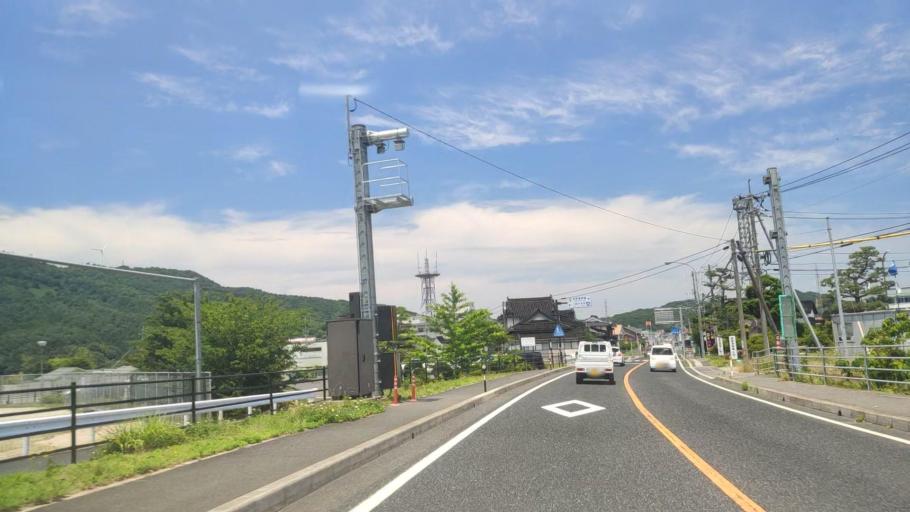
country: JP
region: Tottori
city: Tottori
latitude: 35.4098
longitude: 134.2537
